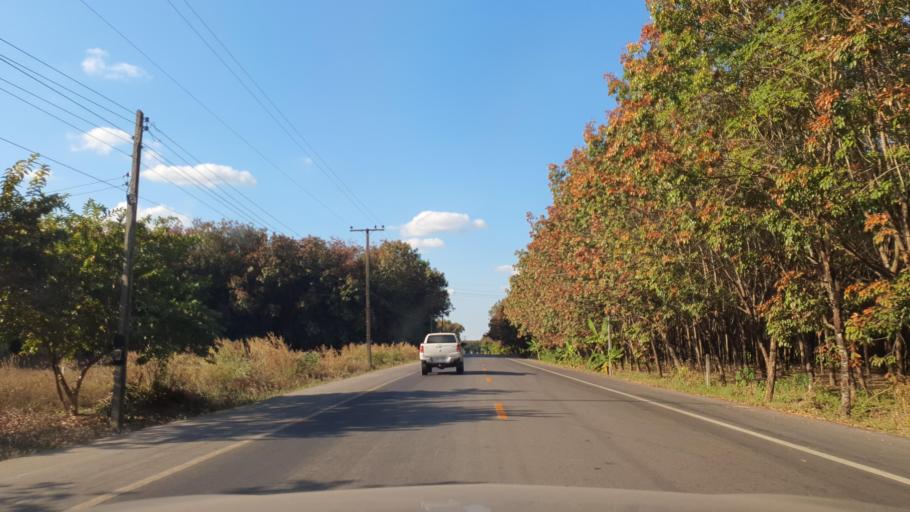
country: TH
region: Nong Khai
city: Bueng Khong Long
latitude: 18.0201
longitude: 103.9988
